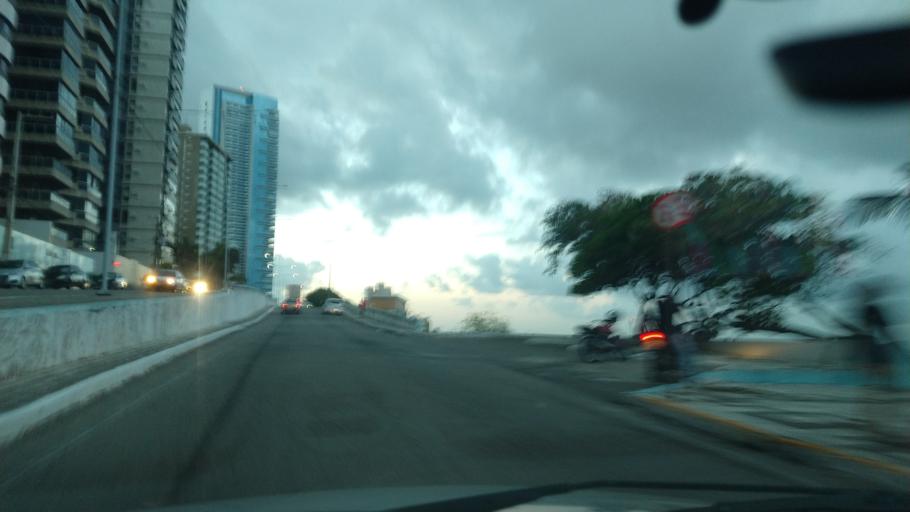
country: BR
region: Rio Grande do Norte
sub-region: Natal
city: Natal
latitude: -5.7832
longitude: -35.1937
